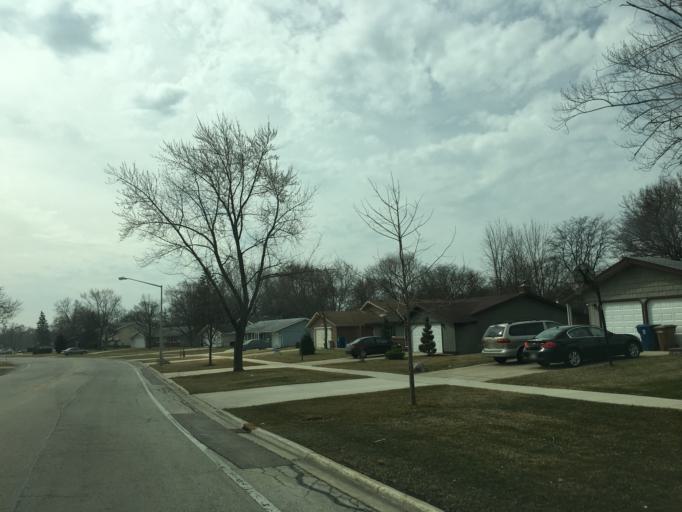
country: US
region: Illinois
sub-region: Cook County
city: Schaumburg
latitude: 42.0247
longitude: -88.1099
